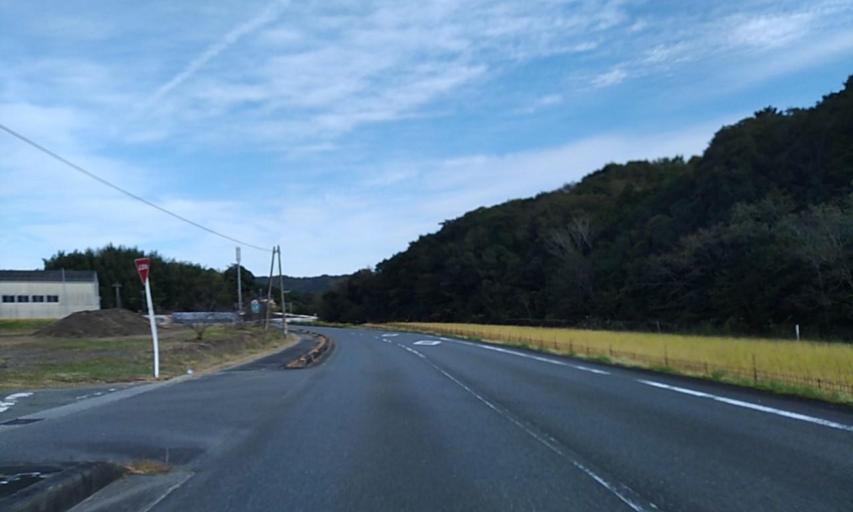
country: JP
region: Mie
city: Ise
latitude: 34.3573
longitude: 136.7617
